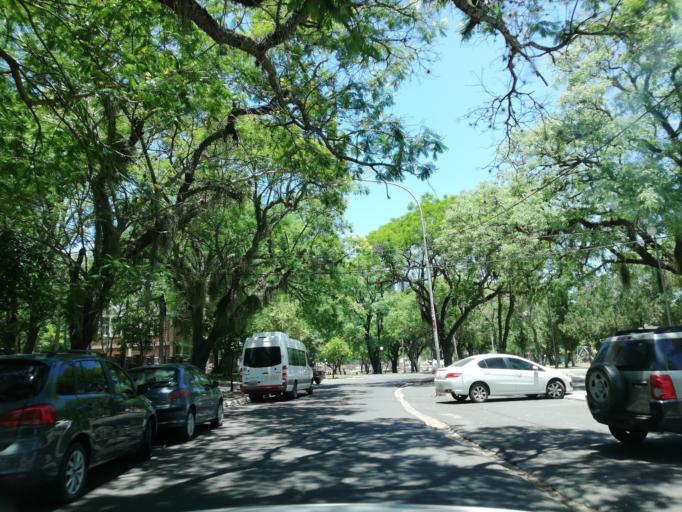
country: AR
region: Corrientes
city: Corrientes
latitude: -27.4591
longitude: -58.8279
